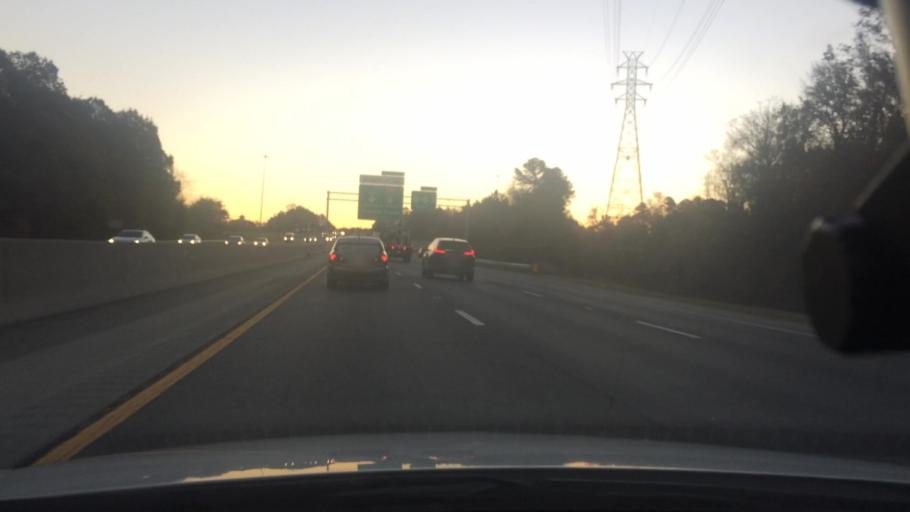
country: US
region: North Carolina
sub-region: Durham County
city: Durham
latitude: 35.9072
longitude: -78.9010
